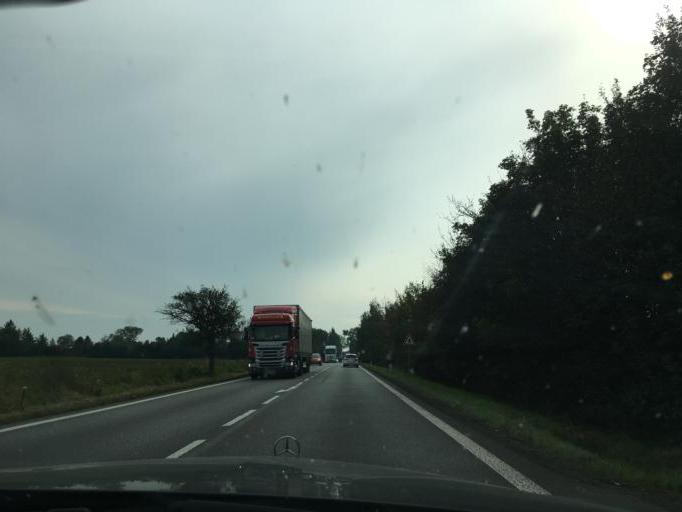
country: CZ
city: Predmerice nad Labem
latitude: 50.2465
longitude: 15.7991
